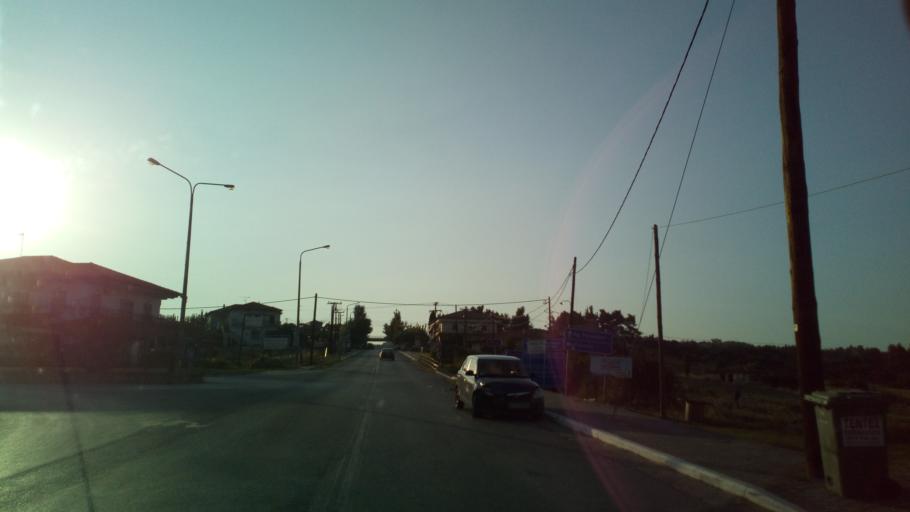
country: GR
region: Central Macedonia
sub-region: Nomos Chalkidikis
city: Pefkochori
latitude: 39.9433
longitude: 23.6662
